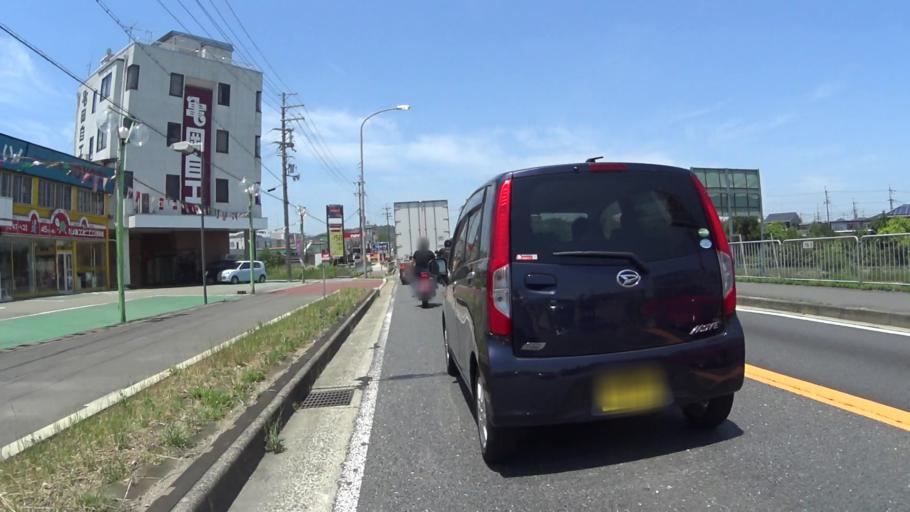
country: JP
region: Kyoto
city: Kameoka
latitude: 35.0049
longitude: 135.5861
